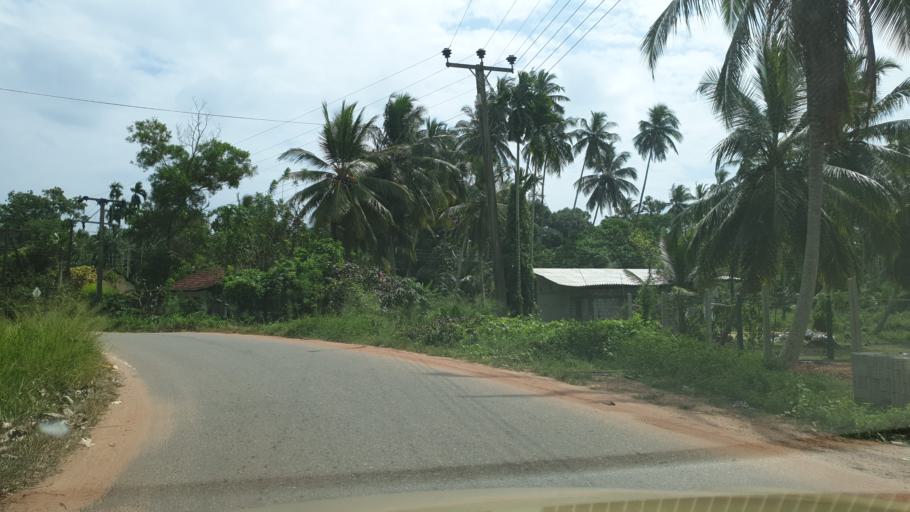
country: LK
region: North Western
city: Kuliyapitiya
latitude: 7.3479
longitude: 79.9798
